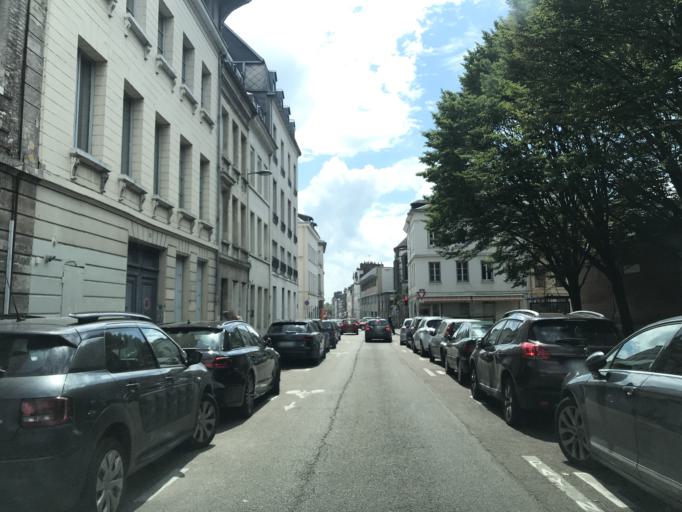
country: FR
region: Haute-Normandie
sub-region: Departement de la Seine-Maritime
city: Rouen
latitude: 49.4454
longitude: 1.0821
